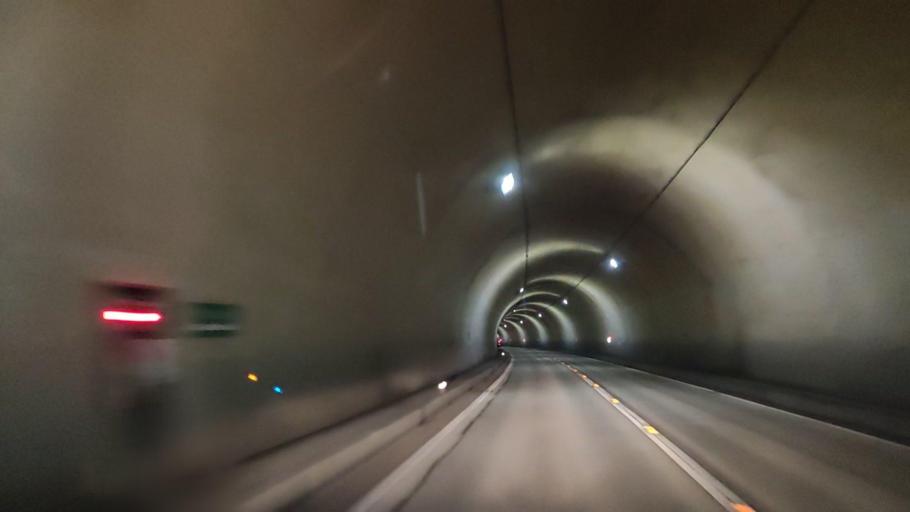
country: JP
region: Tottori
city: Yonago
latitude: 35.2653
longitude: 133.4355
